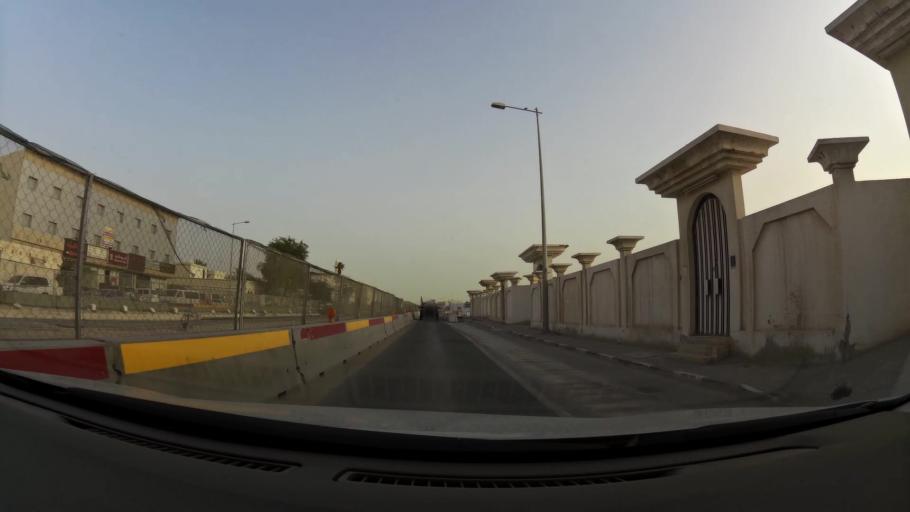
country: QA
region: Baladiyat ar Rayyan
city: Ar Rayyan
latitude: 25.2476
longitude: 51.4527
